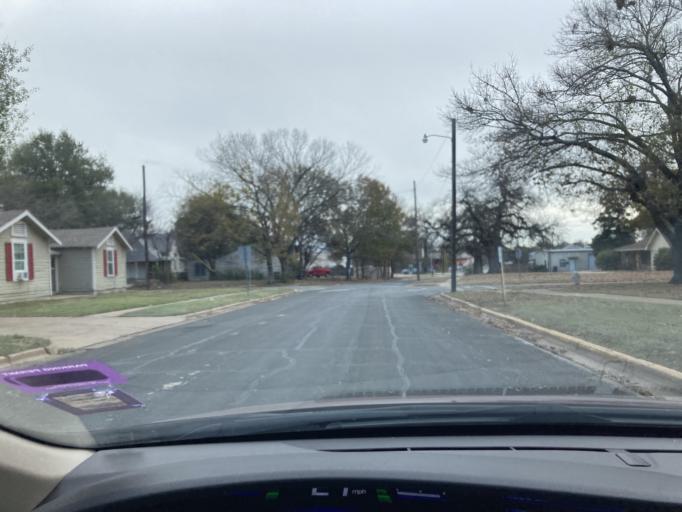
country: US
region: Texas
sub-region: Navarro County
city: Corsicana
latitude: 32.0895
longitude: -96.4713
